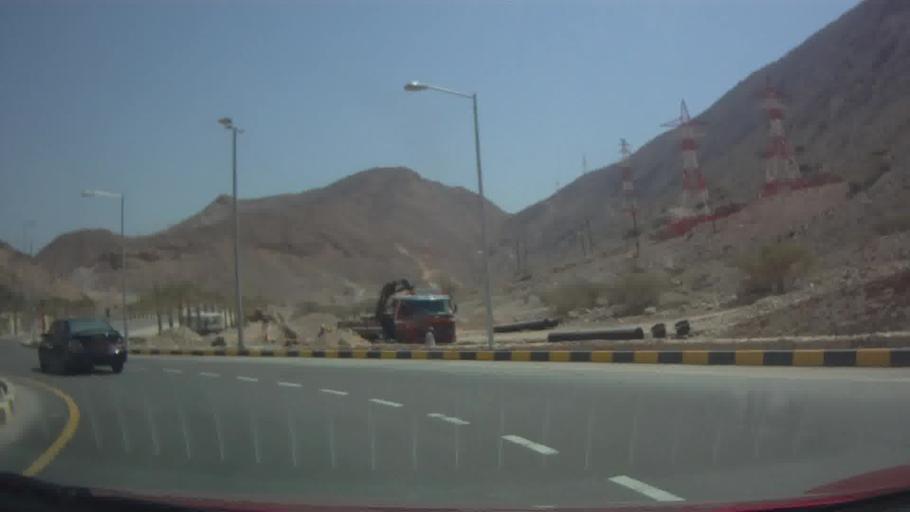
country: OM
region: Muhafazat Masqat
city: Muscat
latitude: 23.5410
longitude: 58.6313
